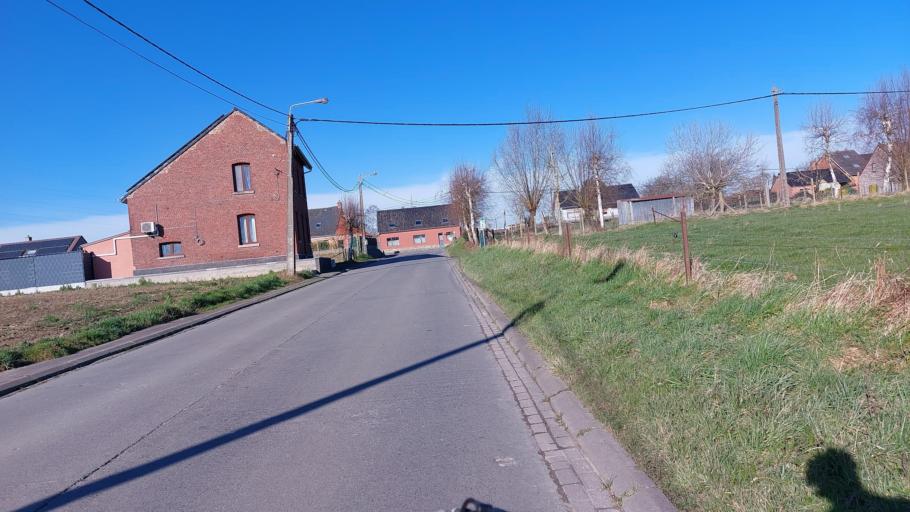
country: BE
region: Wallonia
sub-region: Province du Hainaut
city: Beloeil
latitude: 50.5725
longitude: 3.7634
